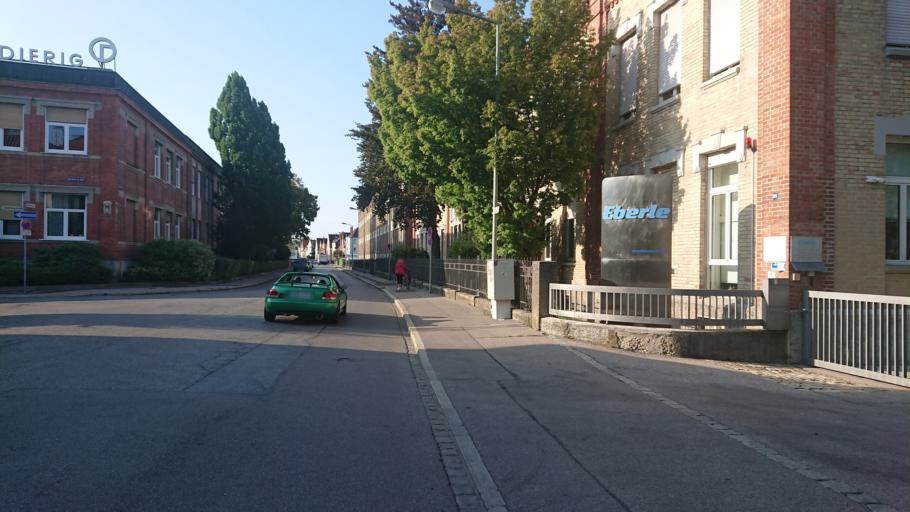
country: DE
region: Bavaria
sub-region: Swabia
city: Augsburg
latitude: 48.3665
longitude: 10.8735
